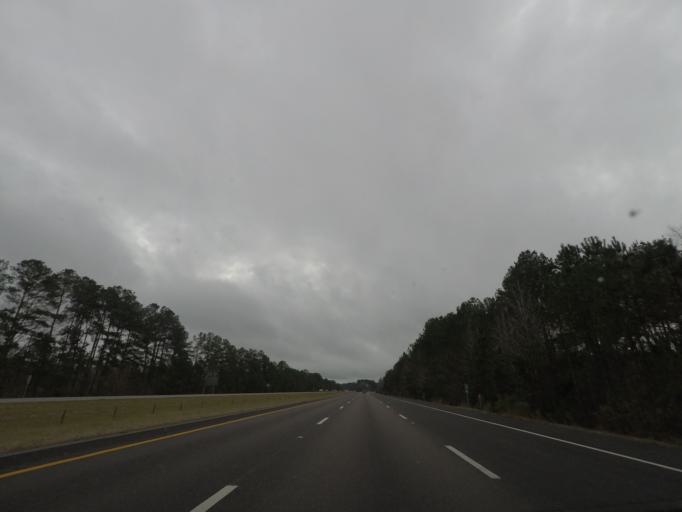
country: US
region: South Carolina
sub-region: Orangeburg County
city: Holly Hill
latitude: 33.4550
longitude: -80.4797
